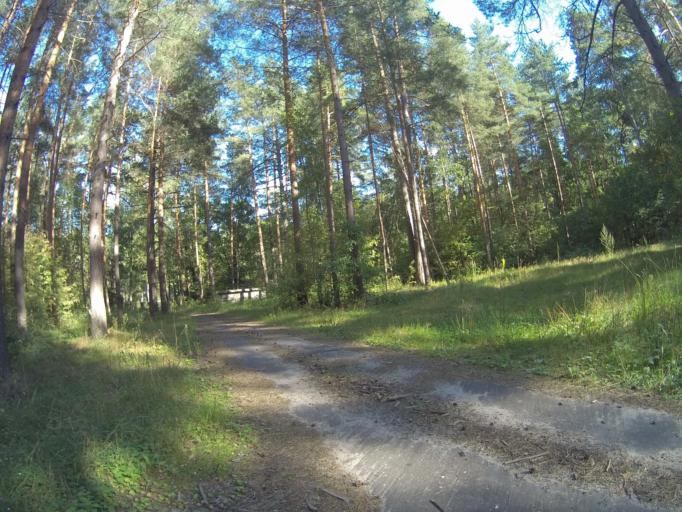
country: RU
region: Vladimir
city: Kommunar
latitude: 56.0724
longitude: 40.4436
